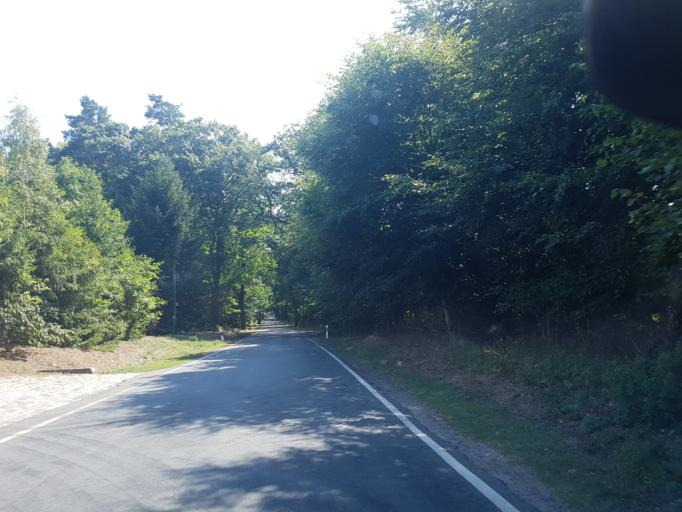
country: DE
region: Brandenburg
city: Wiesenburg
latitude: 52.0231
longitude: 12.3772
